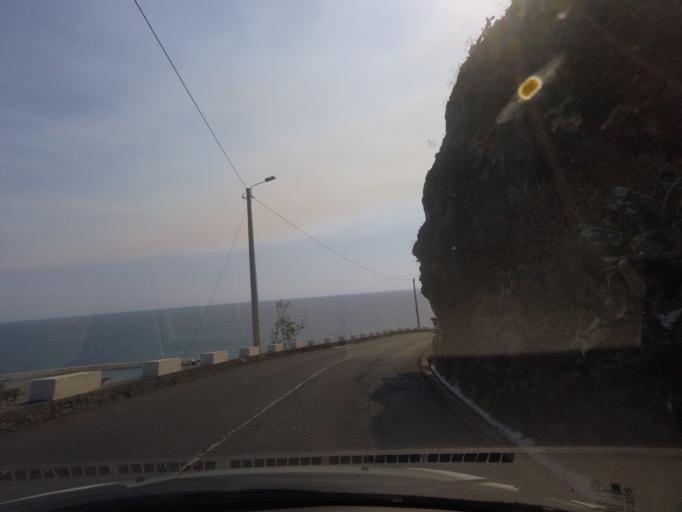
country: PT
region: Madeira
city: Ribeira Brava
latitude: 32.6719
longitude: -17.0660
